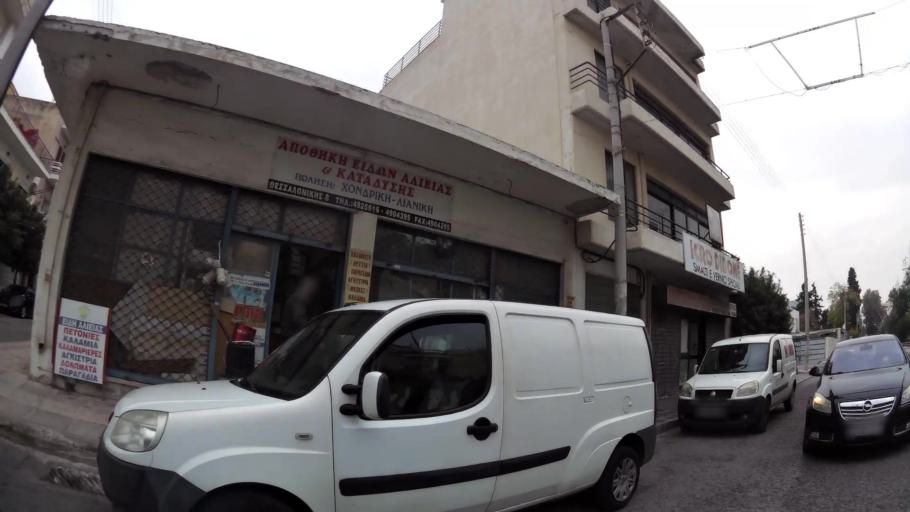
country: GR
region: Attica
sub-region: Nomos Piraios
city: Agios Ioannis Rentis
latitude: 37.9656
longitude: 23.6626
